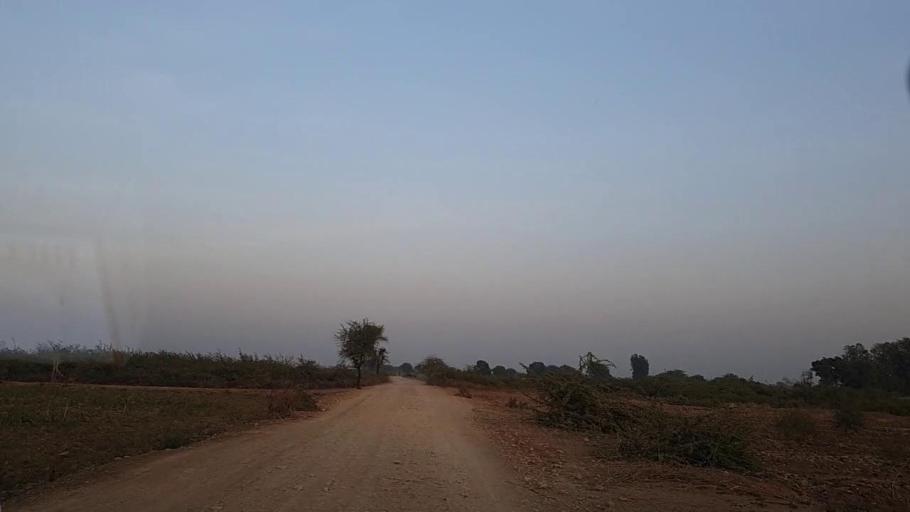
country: PK
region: Sindh
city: Tando Ghulam Ali
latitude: 25.1573
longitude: 68.9283
